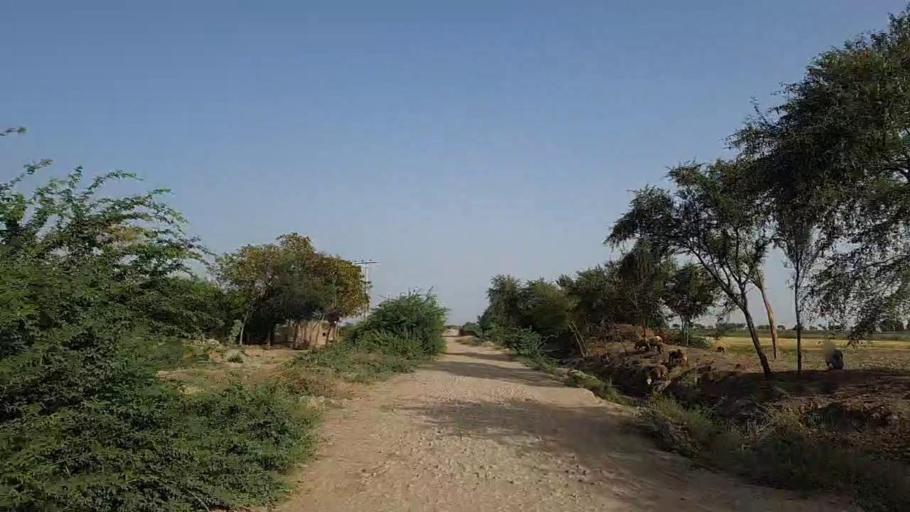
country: PK
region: Sindh
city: Jati
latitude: 24.2623
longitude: 68.1724
